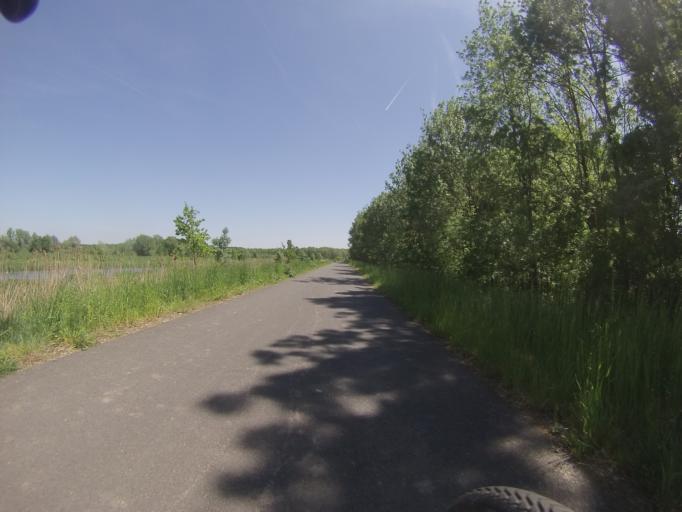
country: CZ
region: South Moravian
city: Vranovice
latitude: 48.9198
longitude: 16.5932
